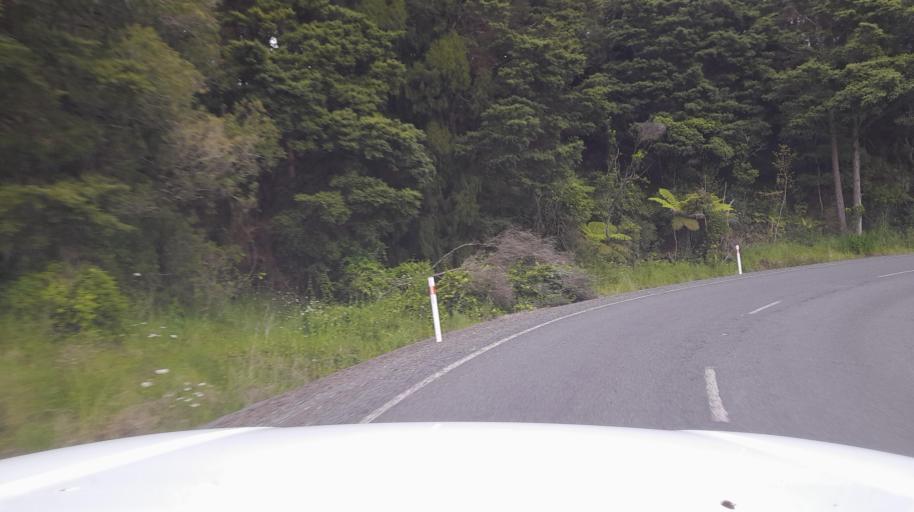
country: NZ
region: Northland
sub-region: Far North District
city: Kaitaia
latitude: -35.3050
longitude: 173.3490
